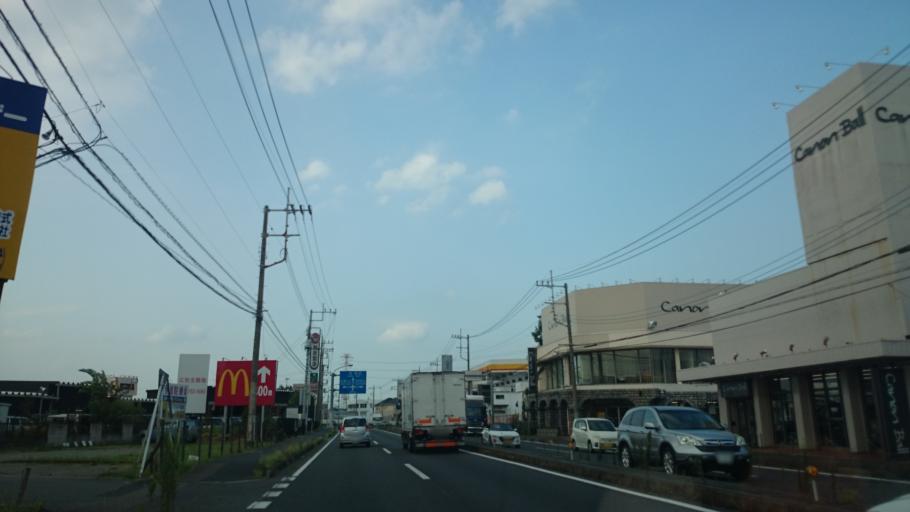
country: JP
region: Saitama
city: Kasukabe
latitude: 35.9688
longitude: 139.7355
